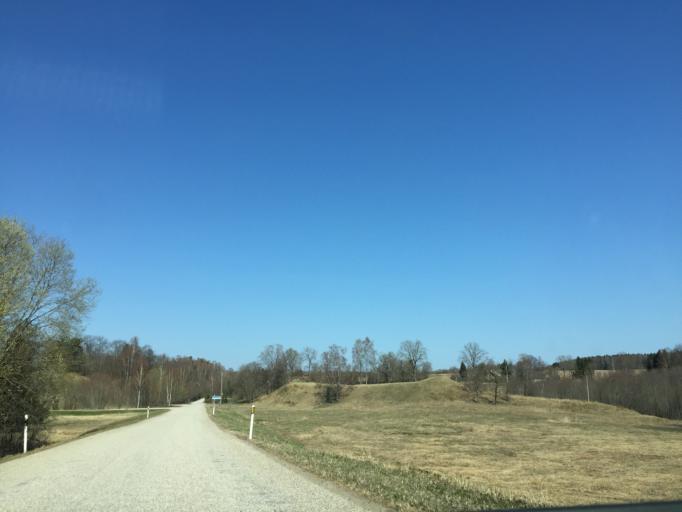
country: EE
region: Tartu
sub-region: Alatskivi vald
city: Kallaste
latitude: 58.6076
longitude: 27.1132
